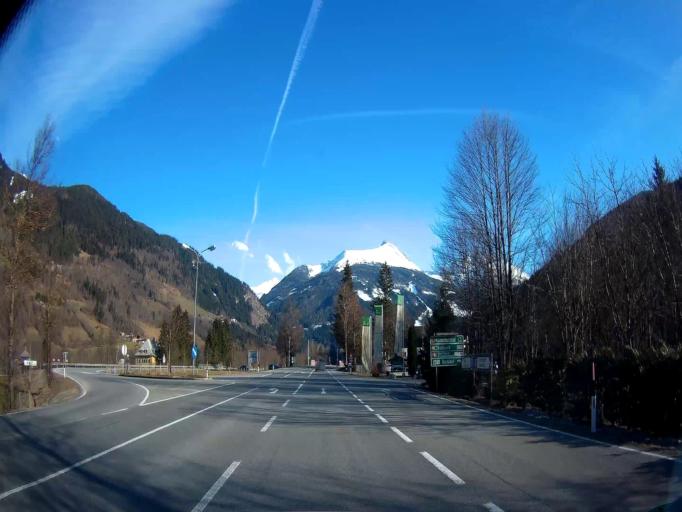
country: AT
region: Salzburg
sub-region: Politischer Bezirk Sankt Johann im Pongau
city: Bad Gastein
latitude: 47.1438
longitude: 13.1205
